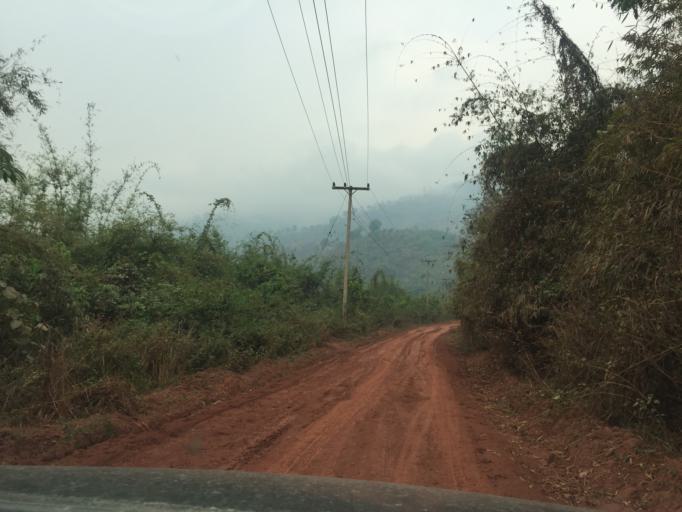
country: TH
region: Nan
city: Bo Kluea
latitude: 18.8462
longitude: 101.4171
